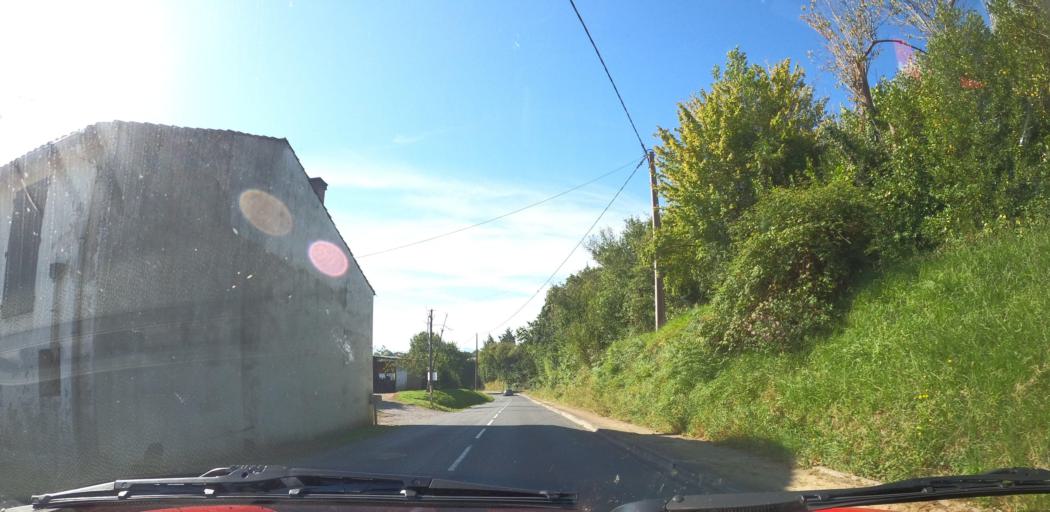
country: FR
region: Aquitaine
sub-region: Departement des Pyrenees-Atlantiques
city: Arbonne
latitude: 43.4171
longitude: -1.5488
